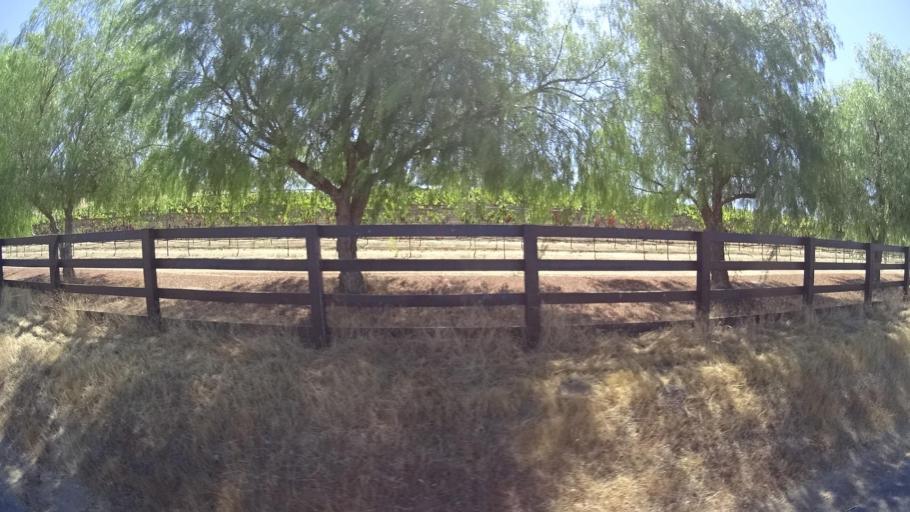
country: US
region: California
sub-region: San Diego County
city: San Diego Country Estates
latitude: 33.0614
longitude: -116.7519
